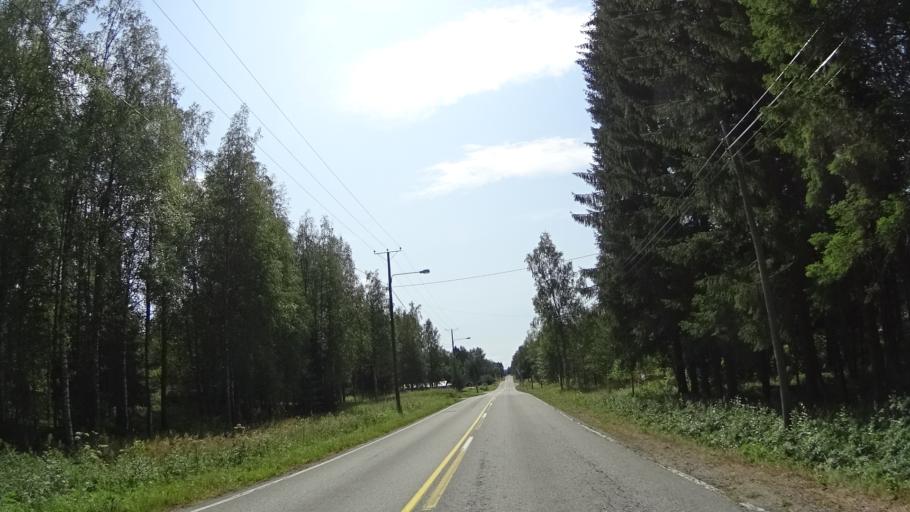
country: FI
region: Pirkanmaa
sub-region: Ylae-Pirkanmaa
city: Maenttae
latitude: 61.8951
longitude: 24.7932
